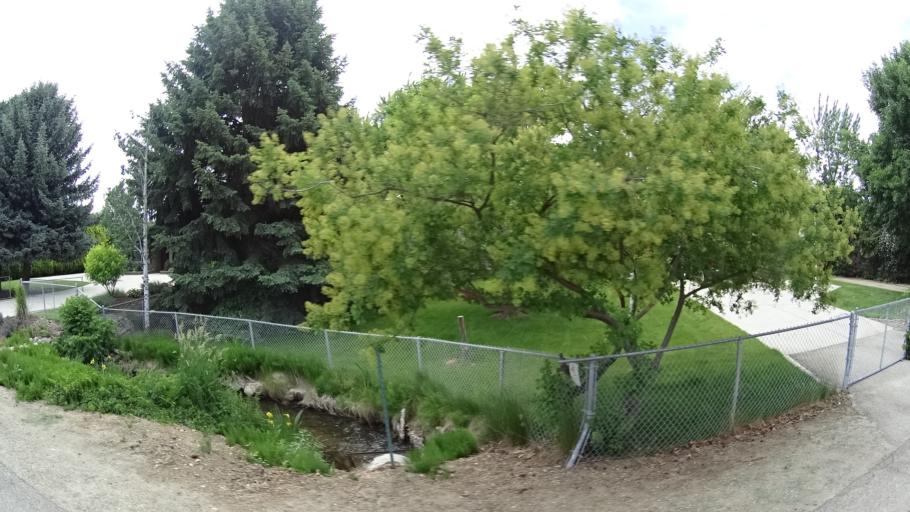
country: US
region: Idaho
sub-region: Ada County
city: Eagle
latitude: 43.6448
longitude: -116.3271
